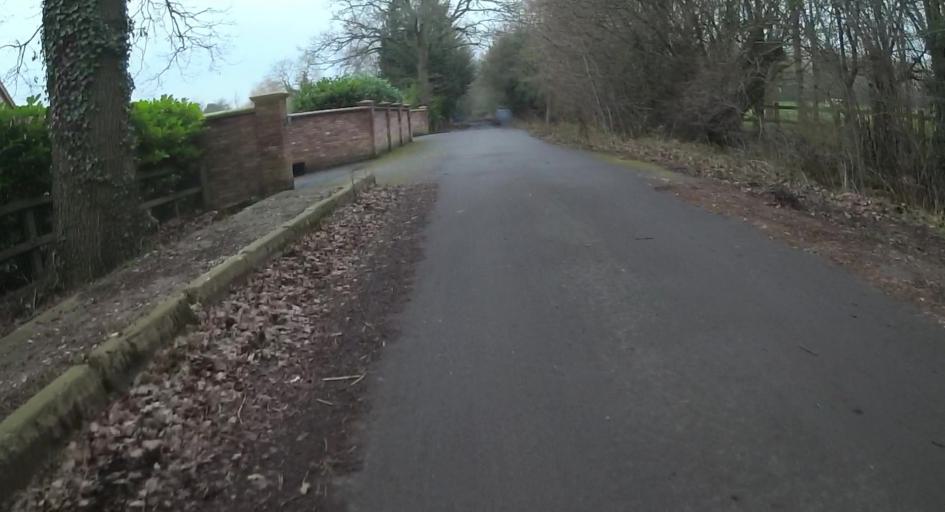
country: GB
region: England
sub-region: Wokingham
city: Barkham
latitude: 51.3913
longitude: -0.8601
